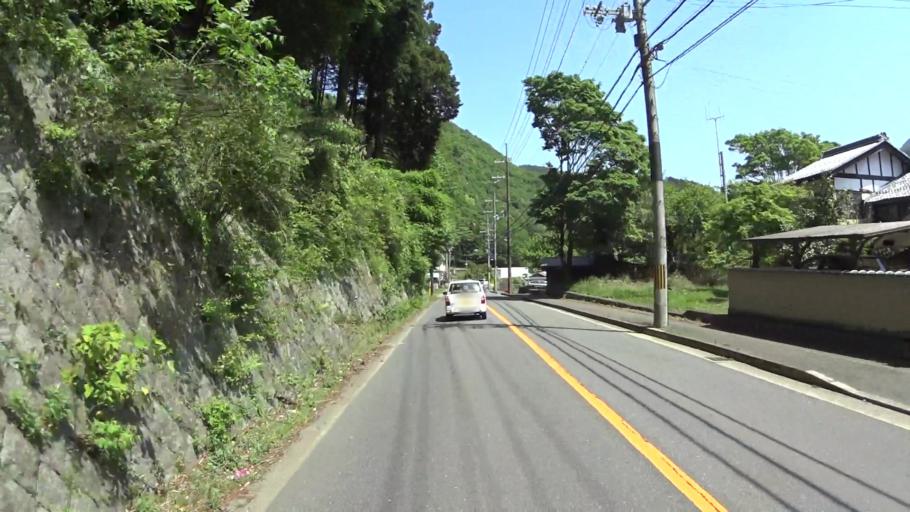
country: JP
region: Kyoto
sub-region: Kyoto-shi
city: Kamigyo-ku
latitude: 35.0815
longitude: 135.8174
